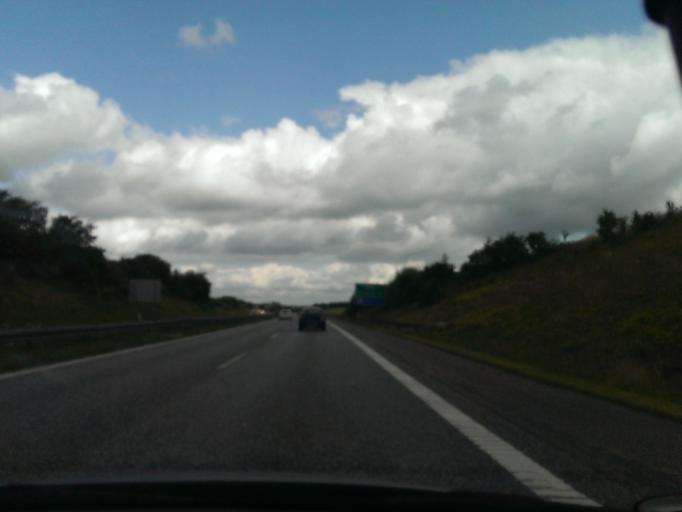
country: DK
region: North Denmark
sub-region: Mariagerfjord Kommune
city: Hobro
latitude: 56.5968
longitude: 9.7619
